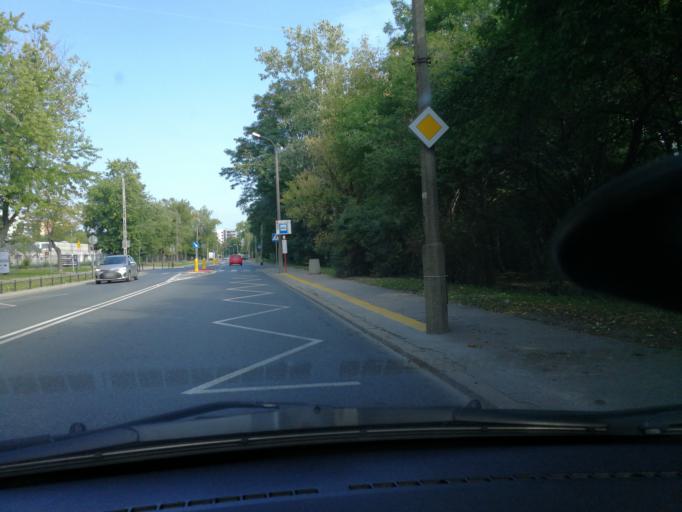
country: PL
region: Masovian Voivodeship
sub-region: Warszawa
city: Bemowo
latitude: 52.2301
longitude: 20.9422
